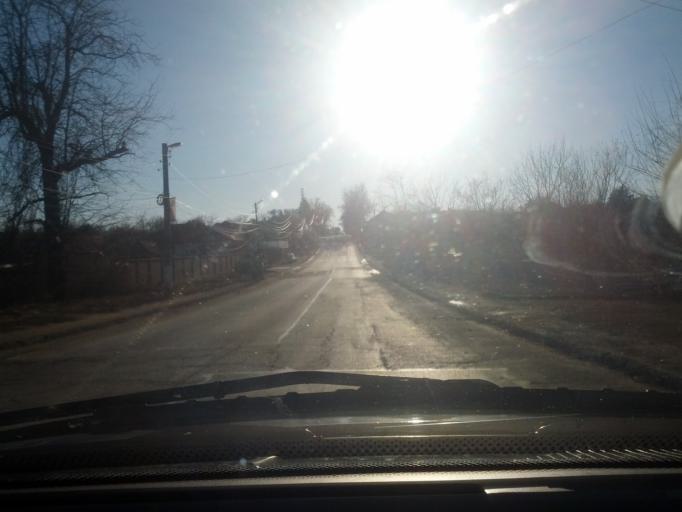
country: BG
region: Vratsa
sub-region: Obshtina Miziya
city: Miziya
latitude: 43.6988
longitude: 23.8180
